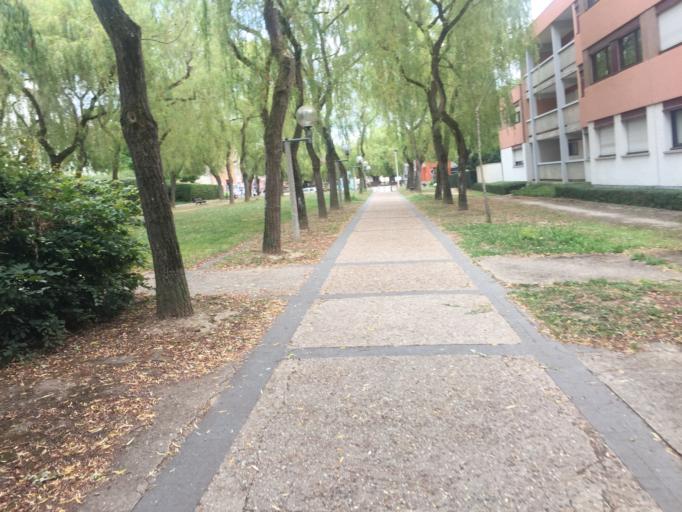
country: FR
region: Ile-de-France
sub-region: Departement des Yvelines
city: Saint-Cyr-l'Ecole
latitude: 48.7837
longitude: 2.0509
